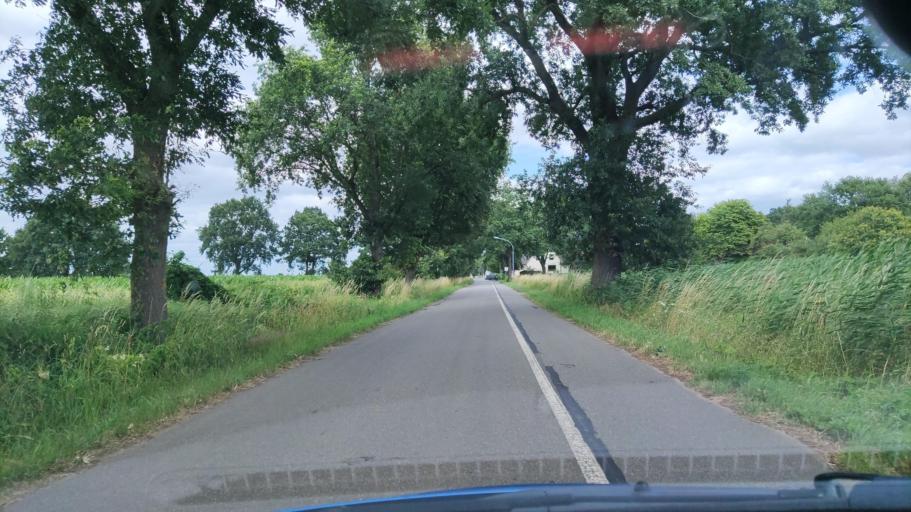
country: DE
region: Lower Saxony
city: Stelle
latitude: 53.4162
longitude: 10.0701
